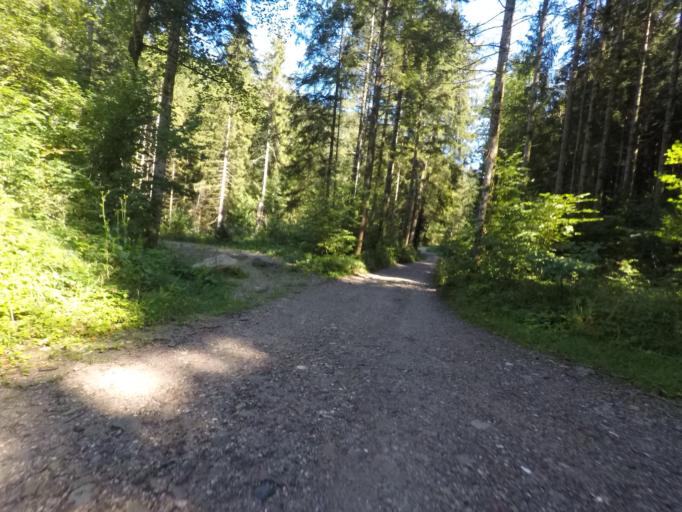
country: DE
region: Bavaria
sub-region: Upper Bavaria
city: Reichersbeuern
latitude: 47.7451
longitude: 11.6557
